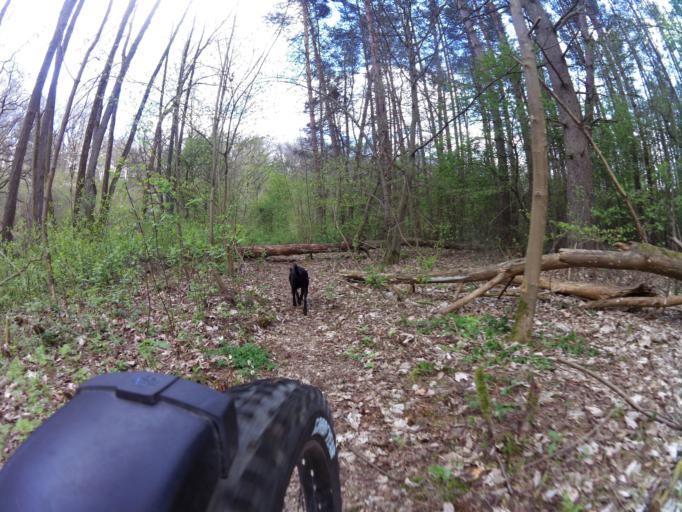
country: PL
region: West Pomeranian Voivodeship
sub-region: Powiat gryficki
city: Ploty
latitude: 53.7916
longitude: 15.2642
